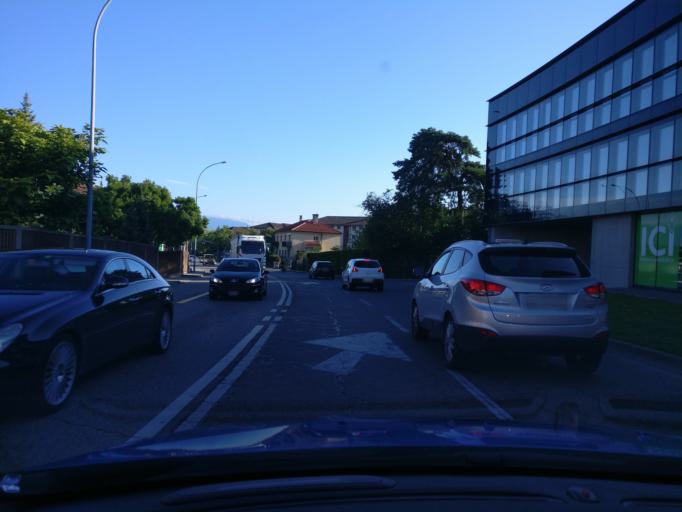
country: CH
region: Geneva
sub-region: Geneva
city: Le Grand-Saconnex
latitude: 46.2347
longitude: 6.1239
